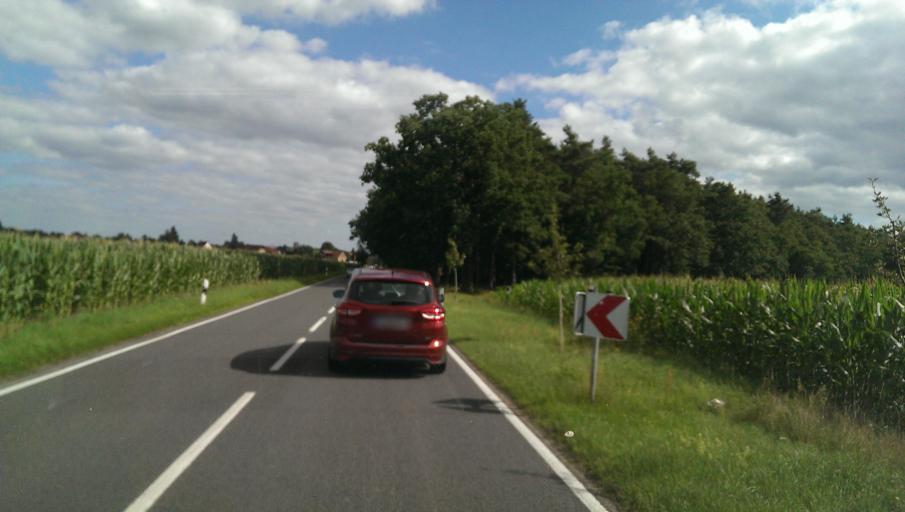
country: DE
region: Saxony-Anhalt
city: Oranienbaum
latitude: 51.8079
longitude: 12.4039
